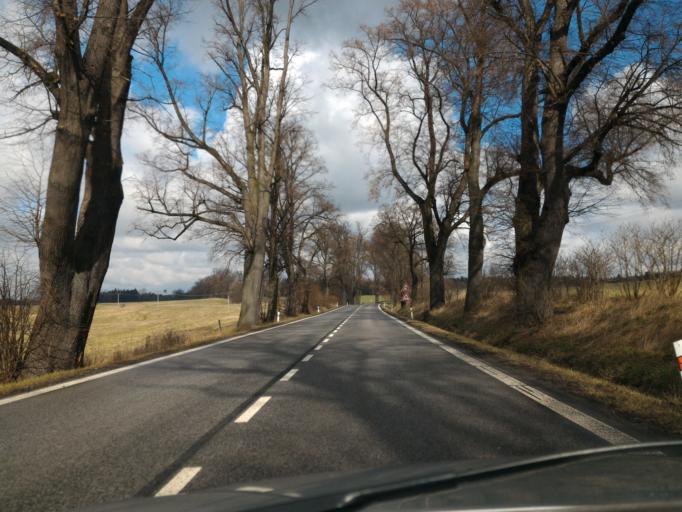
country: PL
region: Silesian Voivodeship
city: Zawidow
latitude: 50.9878
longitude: 15.0774
